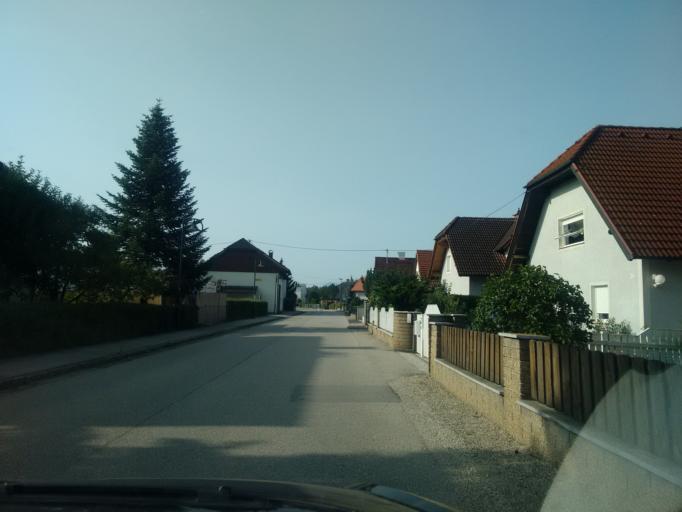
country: AT
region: Upper Austria
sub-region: Wels-Land
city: Gunskirchen
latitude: 48.1250
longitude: 13.9420
